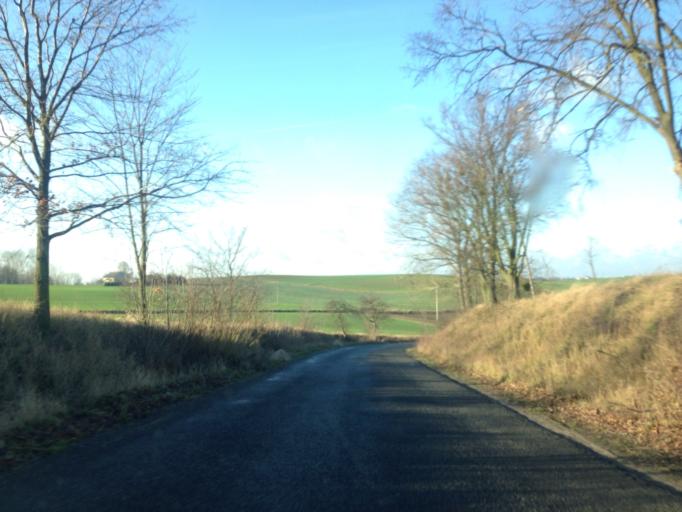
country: PL
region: Kujawsko-Pomorskie
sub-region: Powiat grudziadzki
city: Swiecie nad Osa
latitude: 53.4288
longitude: 19.1012
